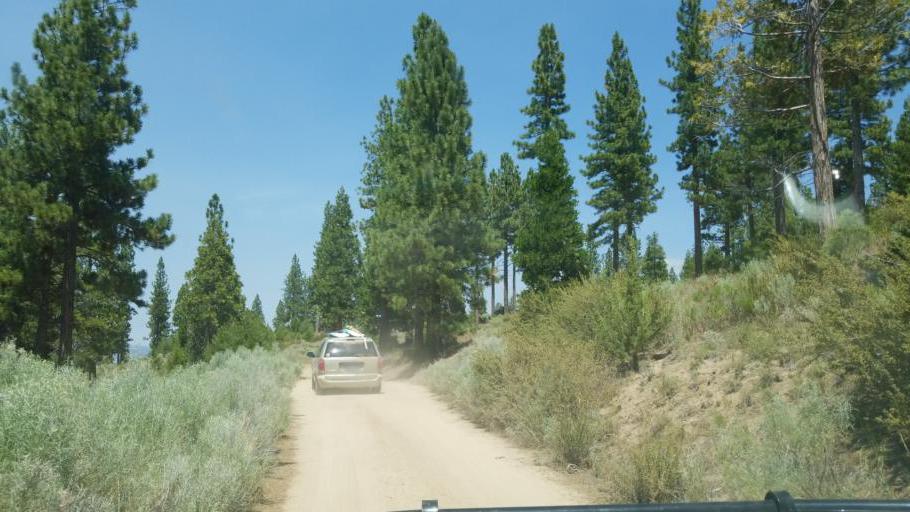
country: US
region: California
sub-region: Lassen County
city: Susanville
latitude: 40.5713
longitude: -120.7533
